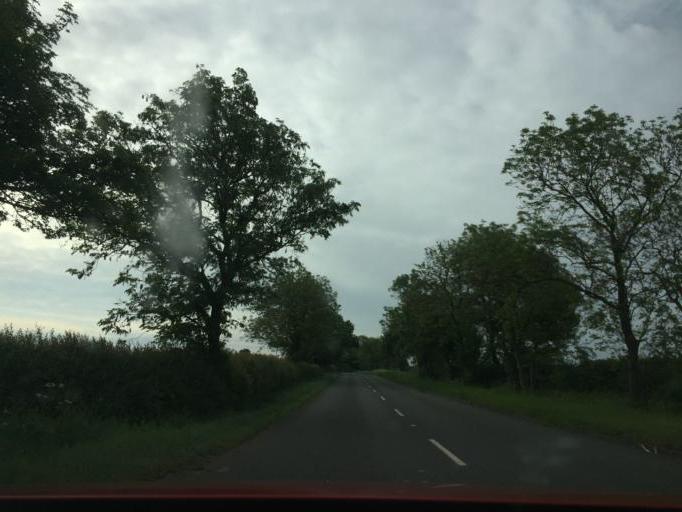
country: GB
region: England
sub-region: Leicestershire
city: Hinckley
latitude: 52.4817
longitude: -1.3339
